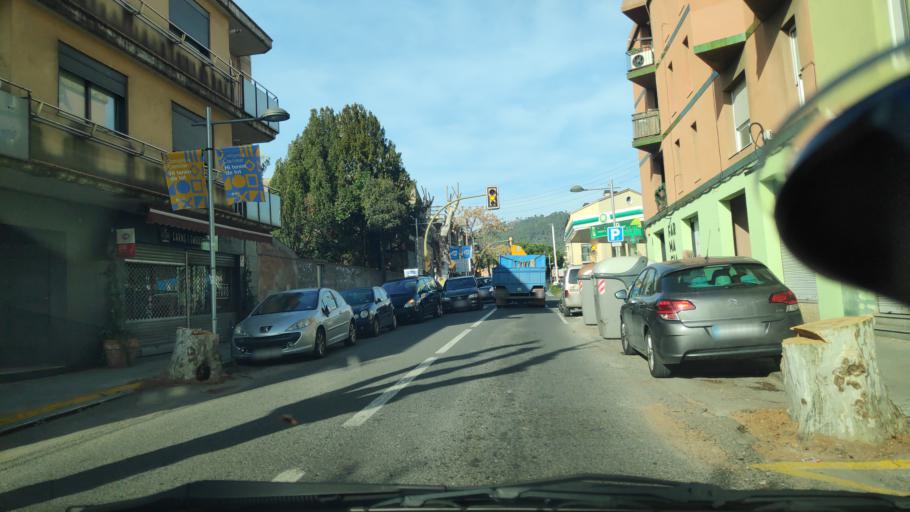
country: ES
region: Catalonia
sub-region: Provincia de Barcelona
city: Castellar del Valles
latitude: 41.6134
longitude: 2.0830
